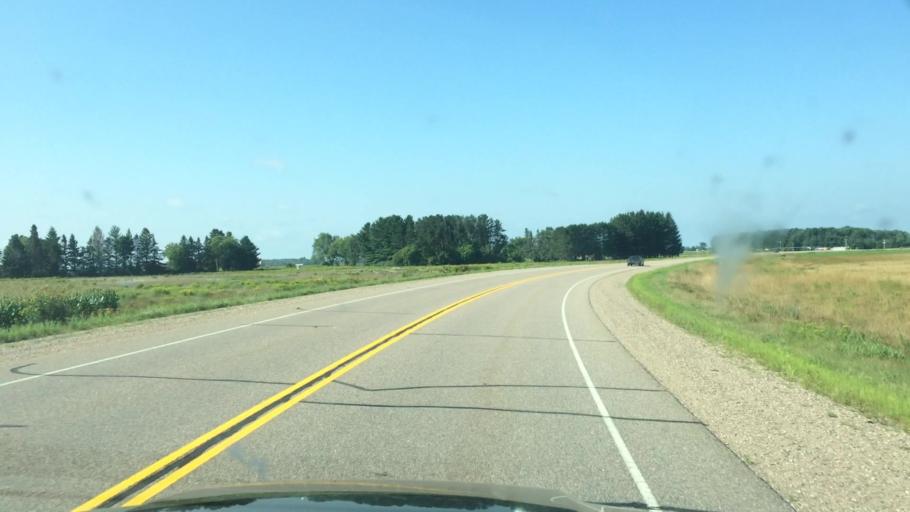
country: US
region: Wisconsin
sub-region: Langlade County
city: Antigo
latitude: 45.1434
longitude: -89.1857
